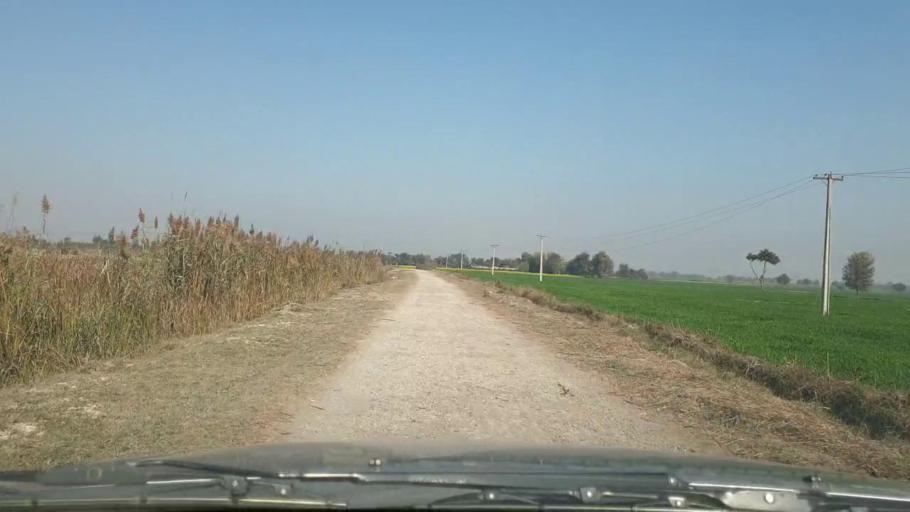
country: PK
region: Sindh
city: Mirpur Mathelo
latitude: 28.0441
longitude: 69.5613
